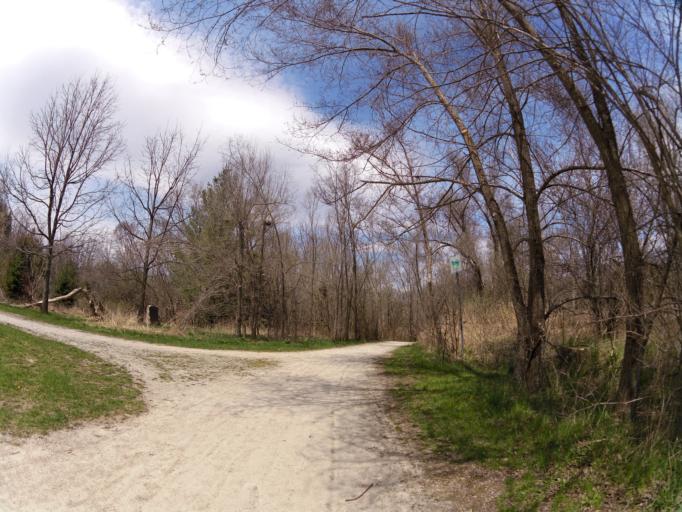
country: CA
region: Ontario
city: Mississauga
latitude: 43.5928
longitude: -79.7180
